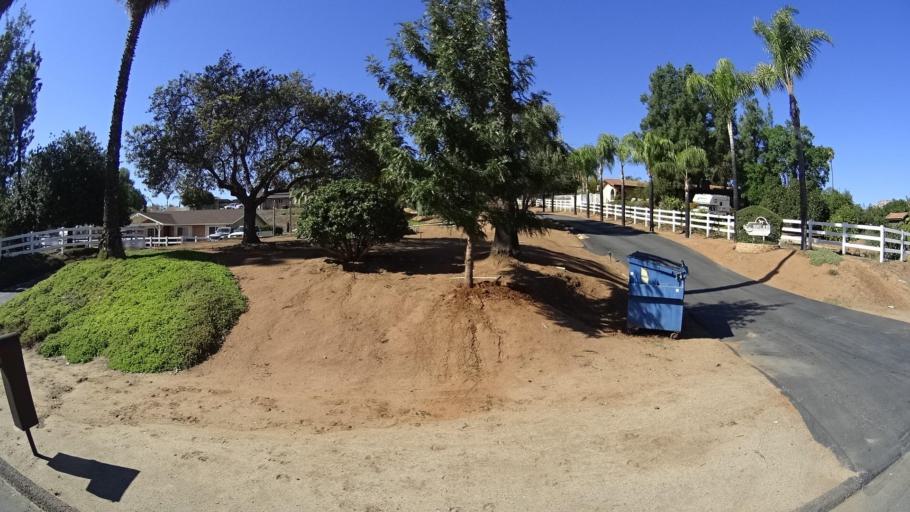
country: US
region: California
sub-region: San Diego County
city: Harbison Canyon
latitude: 32.8671
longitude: -116.8620
